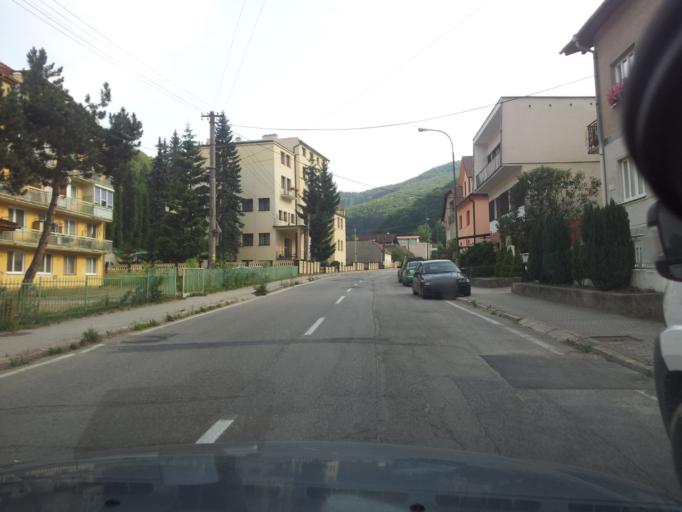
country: SK
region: Nitriansky
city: Trencianske Teplice
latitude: 48.9071
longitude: 18.1666
